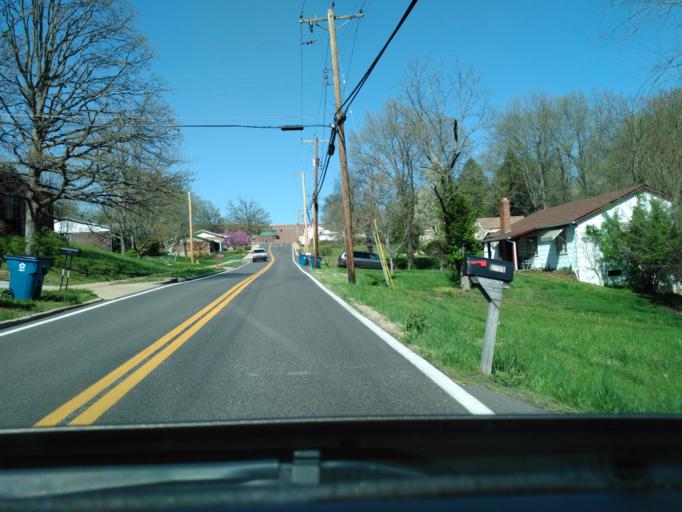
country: US
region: Missouri
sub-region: Saint Louis County
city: Concord
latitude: 38.4981
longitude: -90.3620
